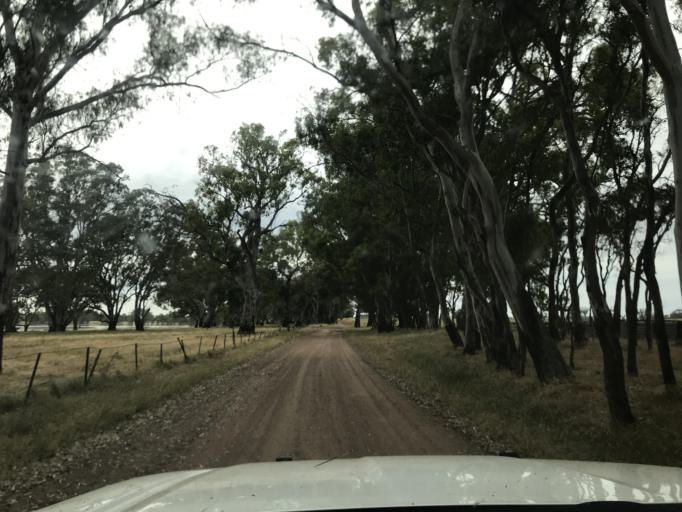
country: AU
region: Victoria
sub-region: Horsham
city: Horsham
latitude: -37.0761
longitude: 141.6635
